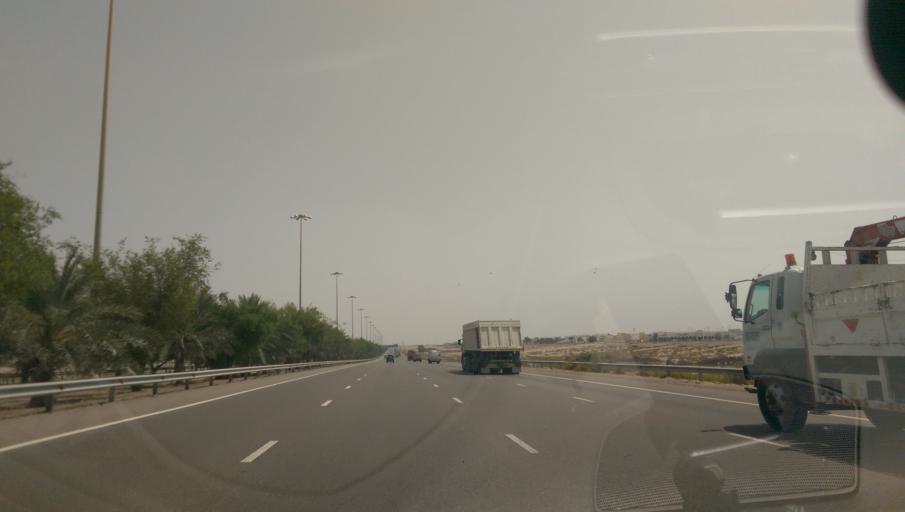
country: AE
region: Abu Dhabi
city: Abu Dhabi
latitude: 24.3493
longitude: 54.6429
